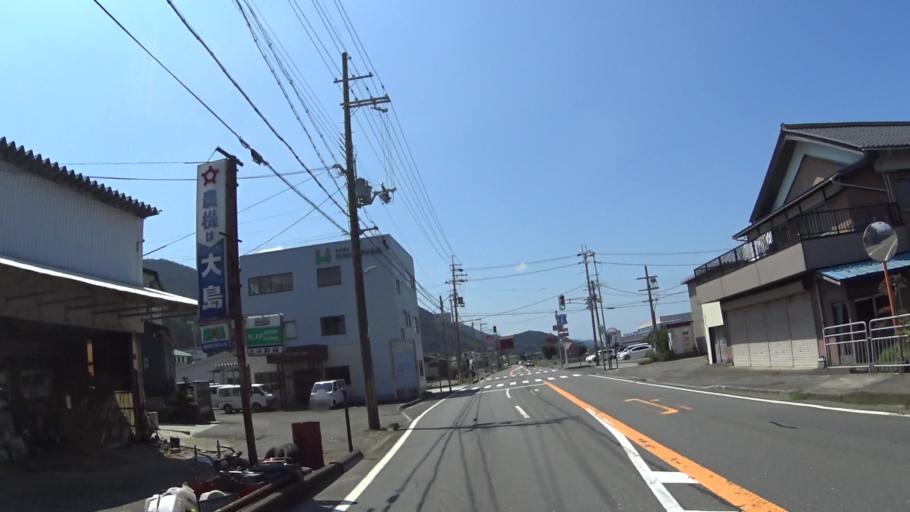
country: JP
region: Fukui
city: Obama
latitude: 35.4636
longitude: 135.8533
